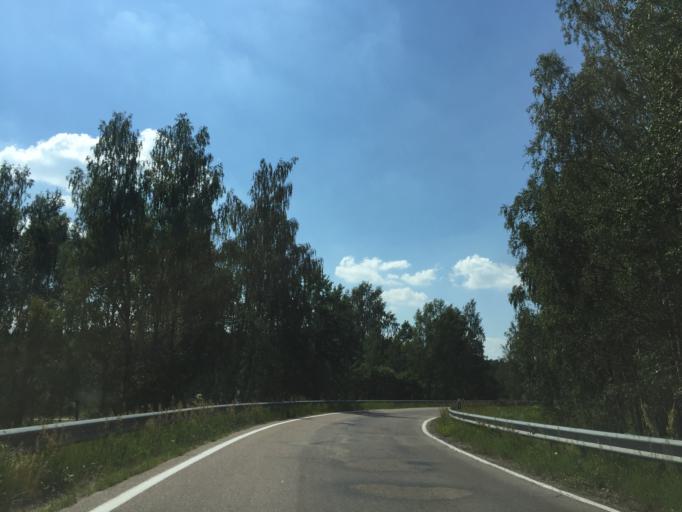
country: LV
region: Babite
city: Pinki
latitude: 56.9518
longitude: 23.9263
